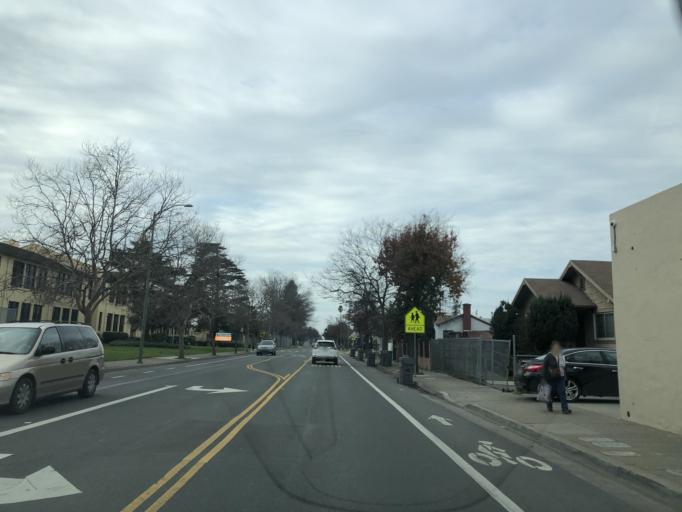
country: US
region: California
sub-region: Alameda County
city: San Leandro
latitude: 37.7469
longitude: -122.1652
